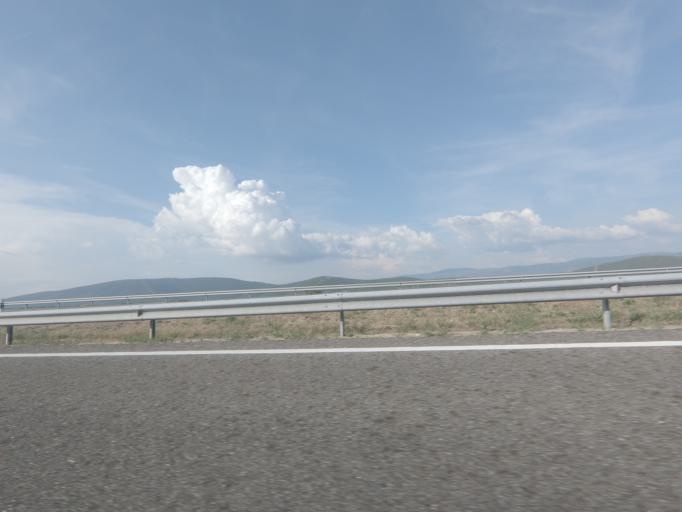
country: ES
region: Galicia
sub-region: Provincia de Ourense
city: Verin
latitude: 41.9615
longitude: -7.5160
